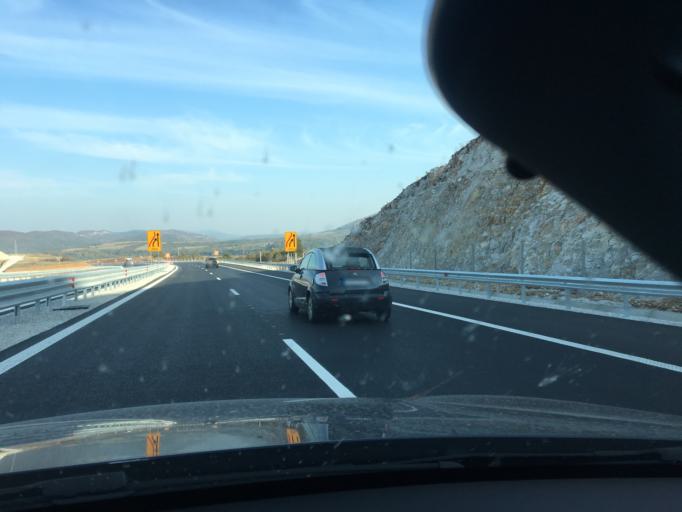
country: BG
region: Lovech
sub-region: Obshtina Yablanitsa
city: Yablanitsa
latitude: 43.0528
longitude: 24.2093
